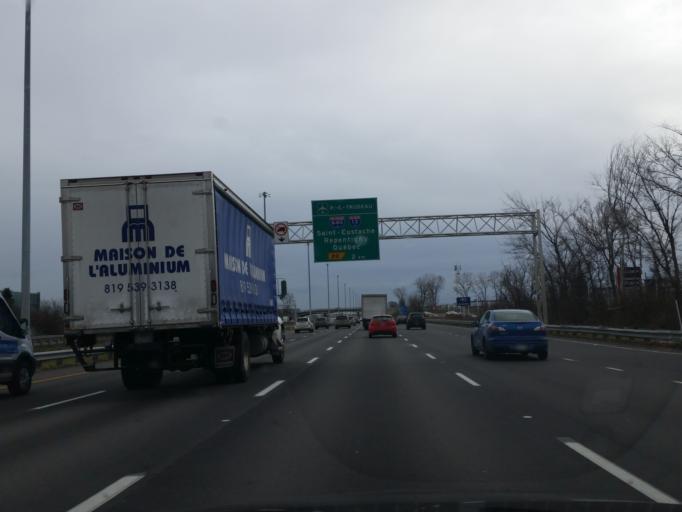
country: CA
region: Quebec
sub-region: Laurentides
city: Blainville
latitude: 45.6428
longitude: -73.8633
